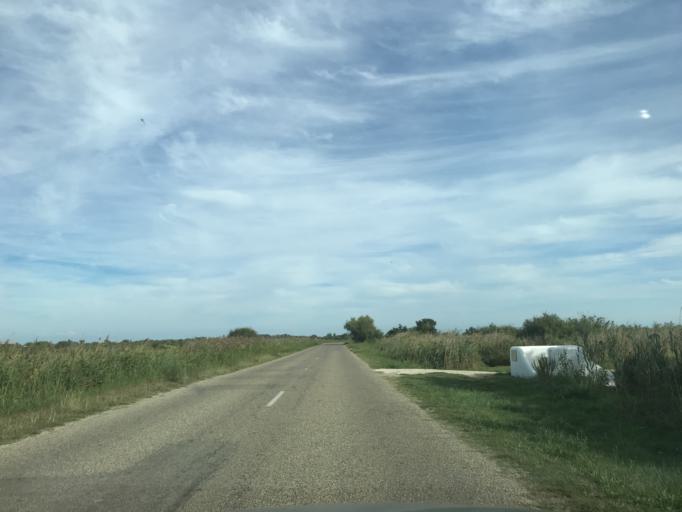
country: FR
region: Provence-Alpes-Cote d'Azur
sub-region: Departement des Bouches-du-Rhone
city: Saintes-Maries-de-la-Mer
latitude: 43.5235
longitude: 4.3828
